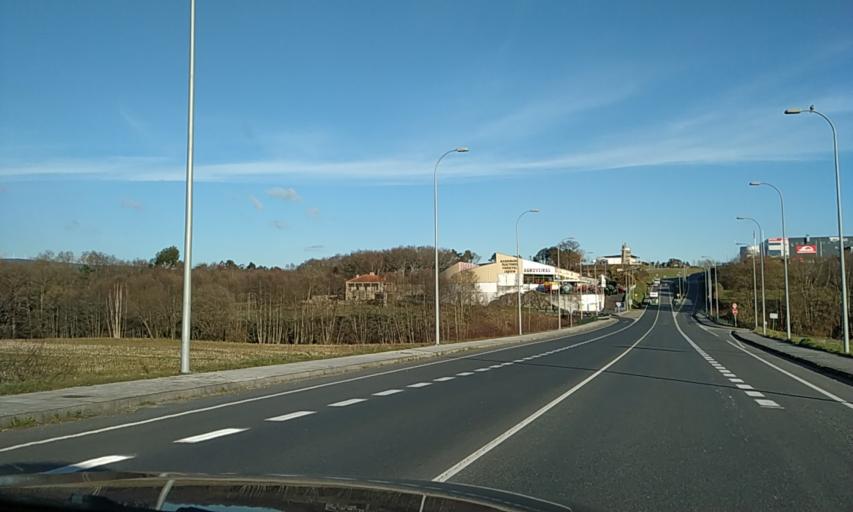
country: ES
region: Galicia
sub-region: Provincia de Pontevedra
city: Silleda
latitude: 42.6945
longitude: -8.2322
